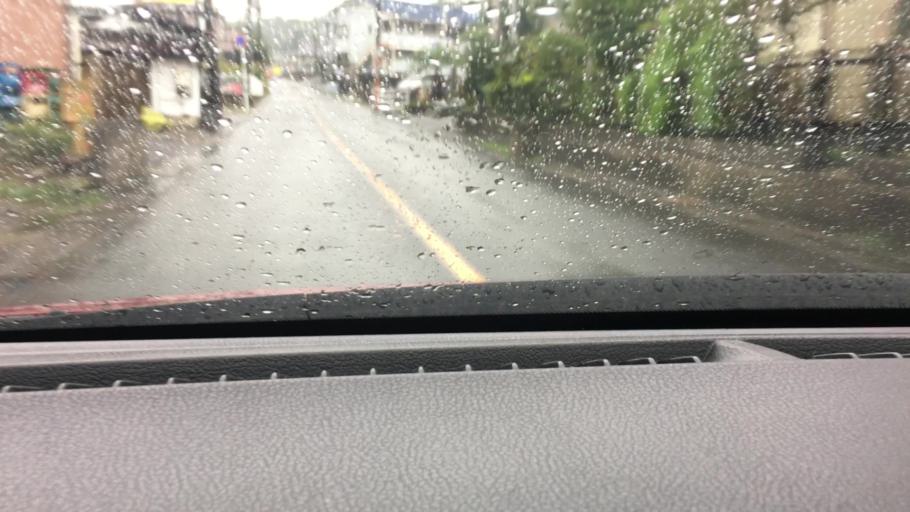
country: JP
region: Chiba
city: Kisarazu
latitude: 35.3736
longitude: 139.9386
